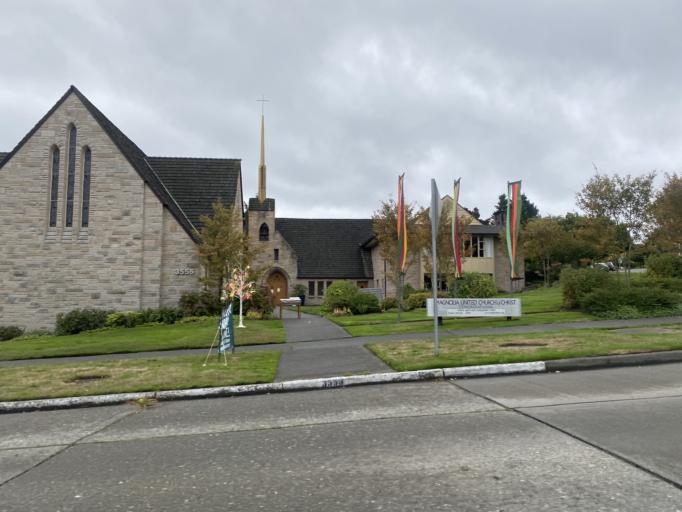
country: US
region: Washington
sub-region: King County
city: Seattle
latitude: 47.6395
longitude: -122.4033
